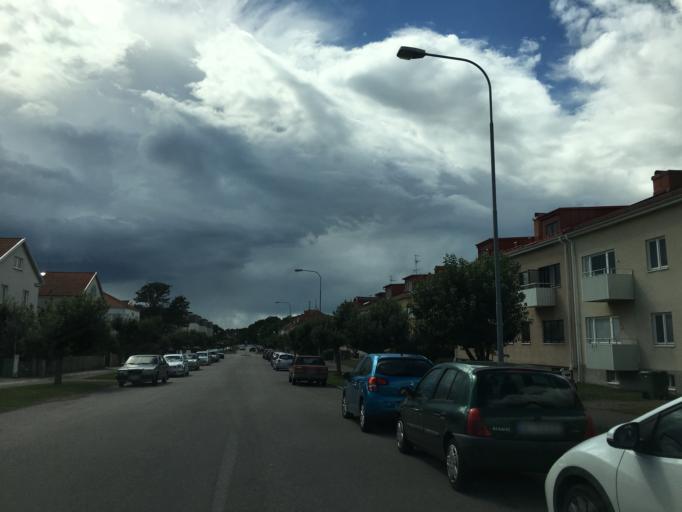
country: SE
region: Kalmar
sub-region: Kalmar Kommun
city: Kalmar
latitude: 56.6567
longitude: 16.3379
